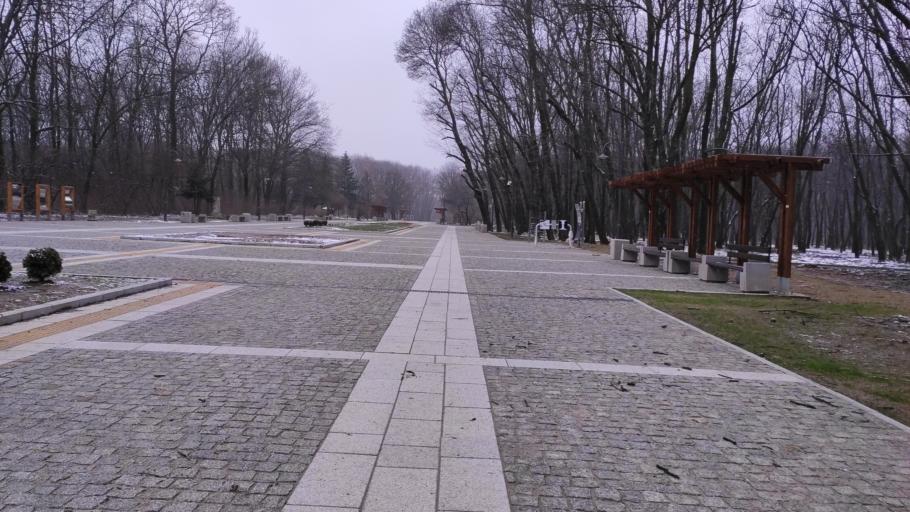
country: BG
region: Sofia-Capital
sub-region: Stolichna Obshtina
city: Sofia
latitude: 42.7116
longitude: 23.2817
